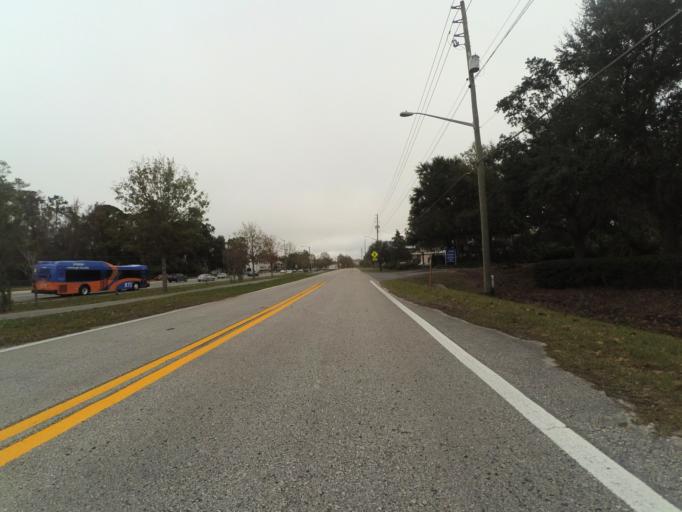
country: US
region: Florida
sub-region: Alachua County
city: Gainesville
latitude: 29.6327
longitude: -82.3599
